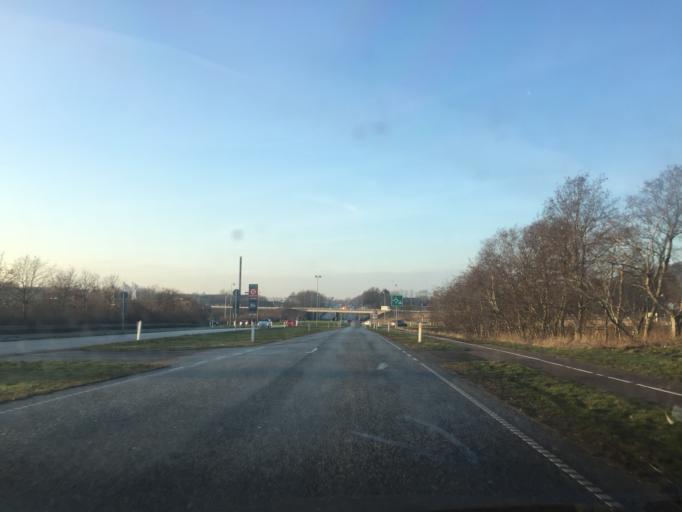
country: DK
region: Zealand
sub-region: Slagelse Kommune
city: Slagelse
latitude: 55.3874
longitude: 11.3659
